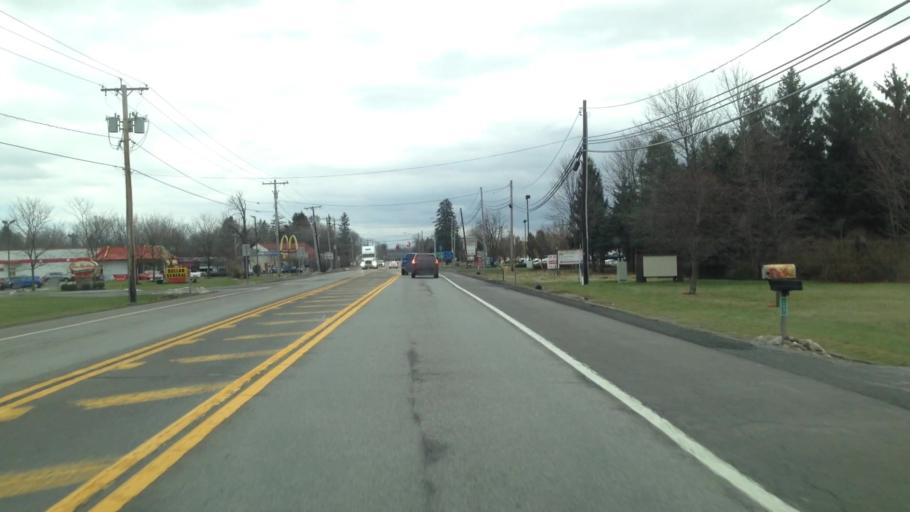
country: US
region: New York
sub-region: Erie County
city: Akron
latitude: 42.9976
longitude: -78.5054
